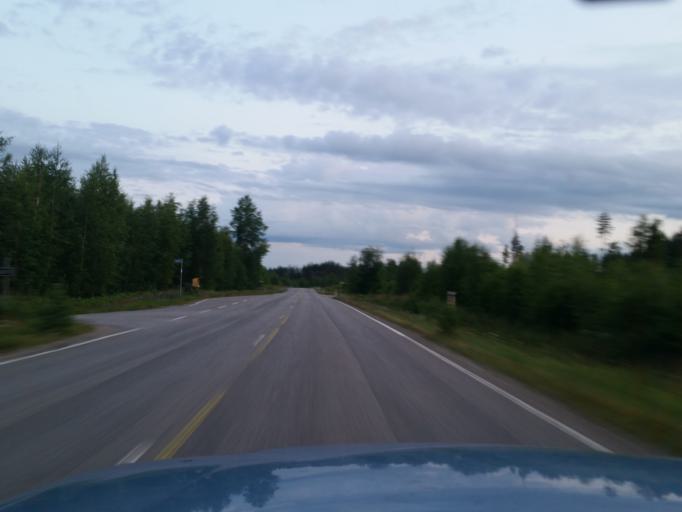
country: FI
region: Southern Savonia
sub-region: Savonlinna
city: Sulkava
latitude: 61.8147
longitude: 28.4328
